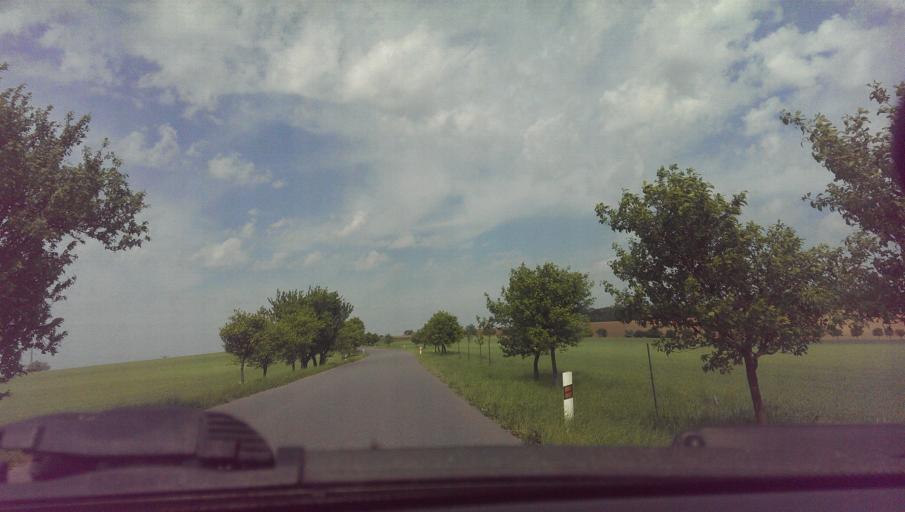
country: CZ
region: Zlin
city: Otrokovice
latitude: 49.2540
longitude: 17.5393
